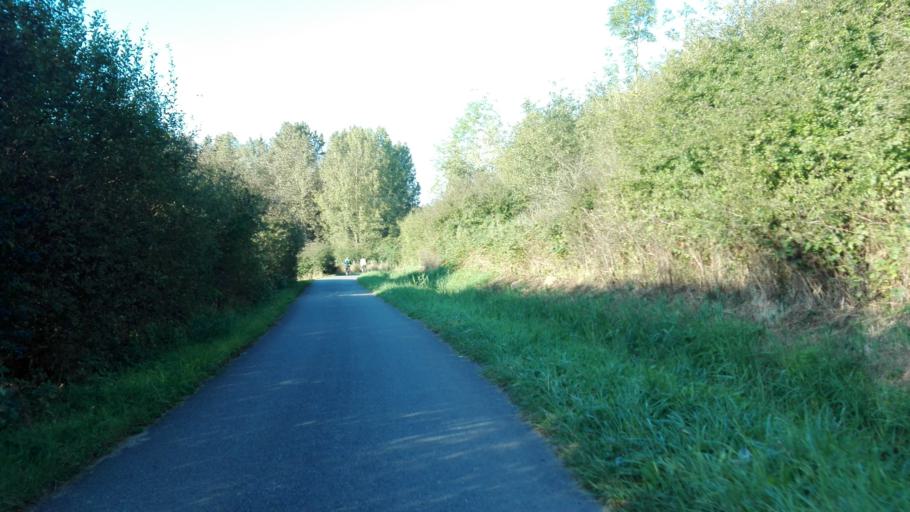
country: FR
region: Nord-Pas-de-Calais
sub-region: Departement du Nord
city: Watten
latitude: 50.8282
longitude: 2.1936
